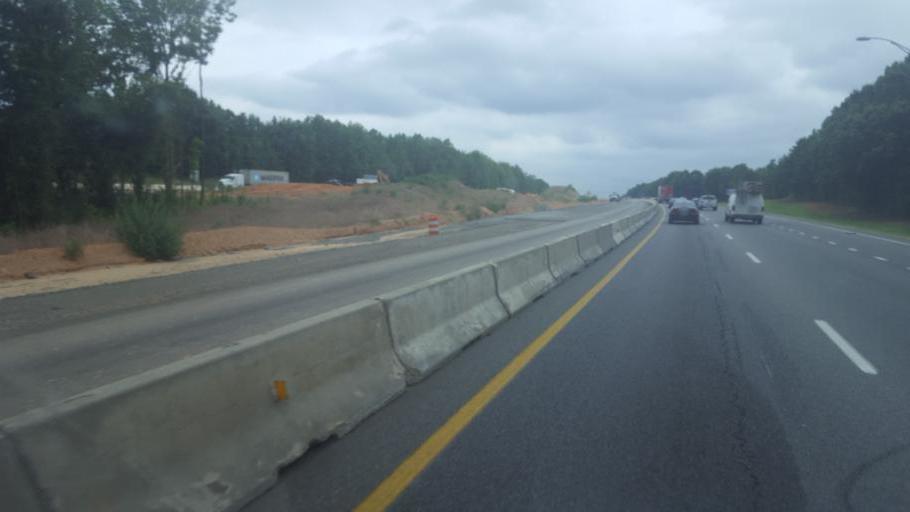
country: US
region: North Carolina
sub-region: Mecklenburg County
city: Cornelius
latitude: 35.4488
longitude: -80.8692
